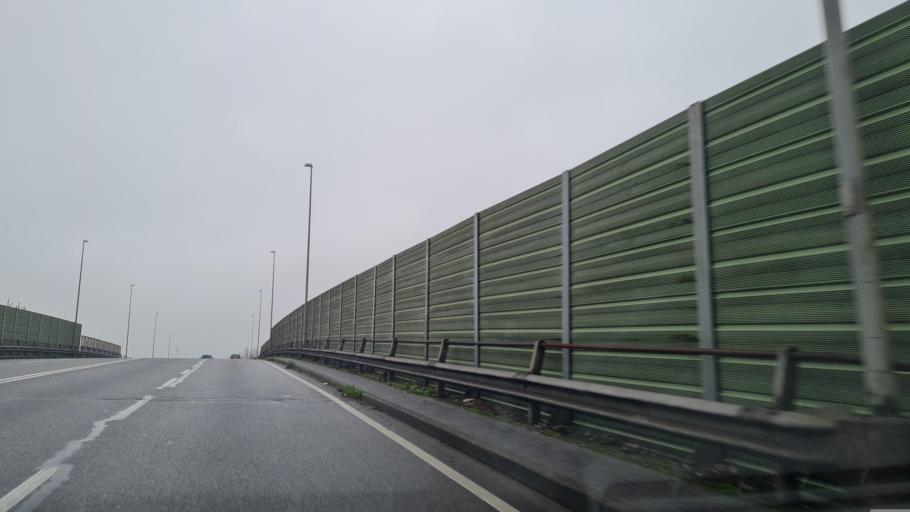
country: IT
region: Tuscany
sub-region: Provincia di Lucca
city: Lucca
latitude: 43.8392
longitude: 10.4762
